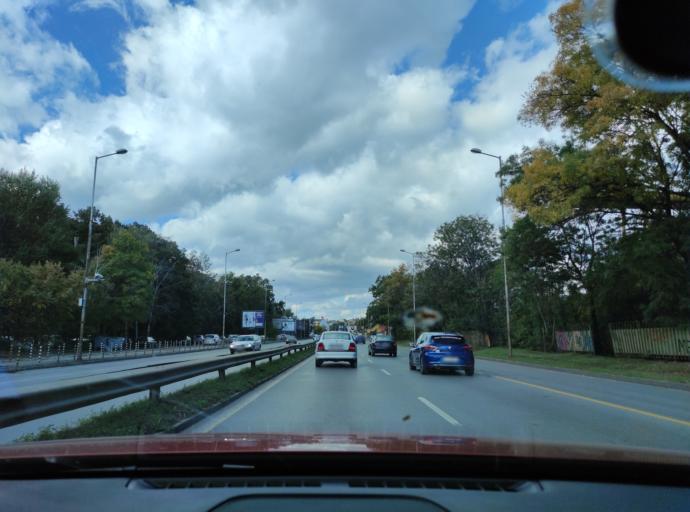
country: BG
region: Sofia-Capital
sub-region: Stolichna Obshtina
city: Sofia
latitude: 42.7025
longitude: 23.3381
